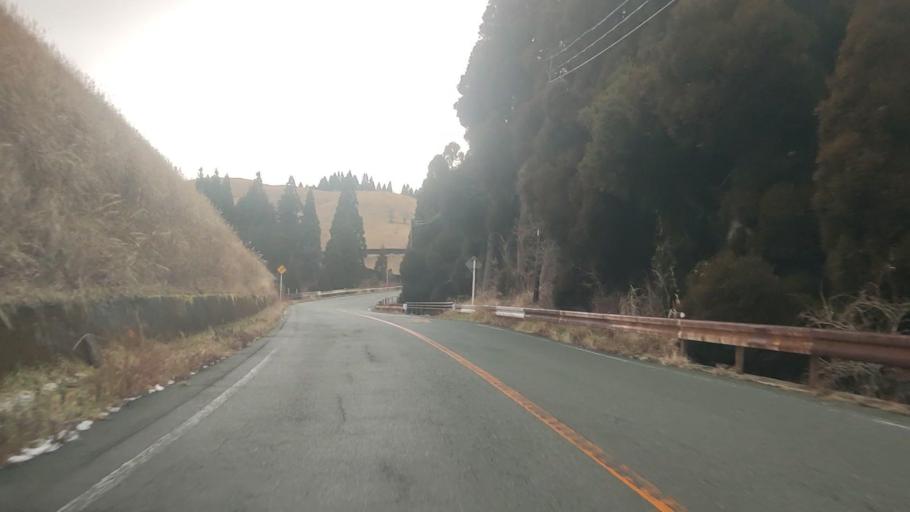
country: JP
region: Kumamoto
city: Aso
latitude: 32.8870
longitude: 131.1703
